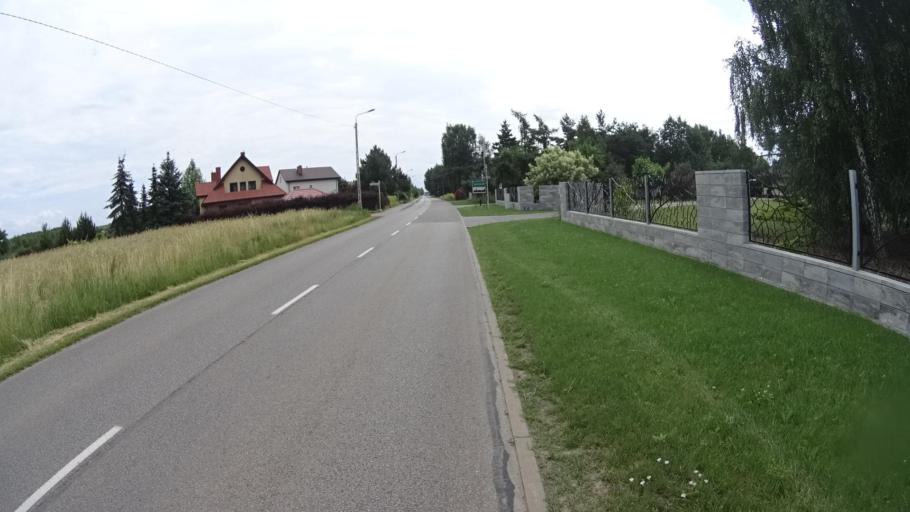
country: PL
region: Masovian Voivodeship
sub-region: Powiat piaseczynski
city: Tarczyn
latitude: 52.0023
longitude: 20.8131
